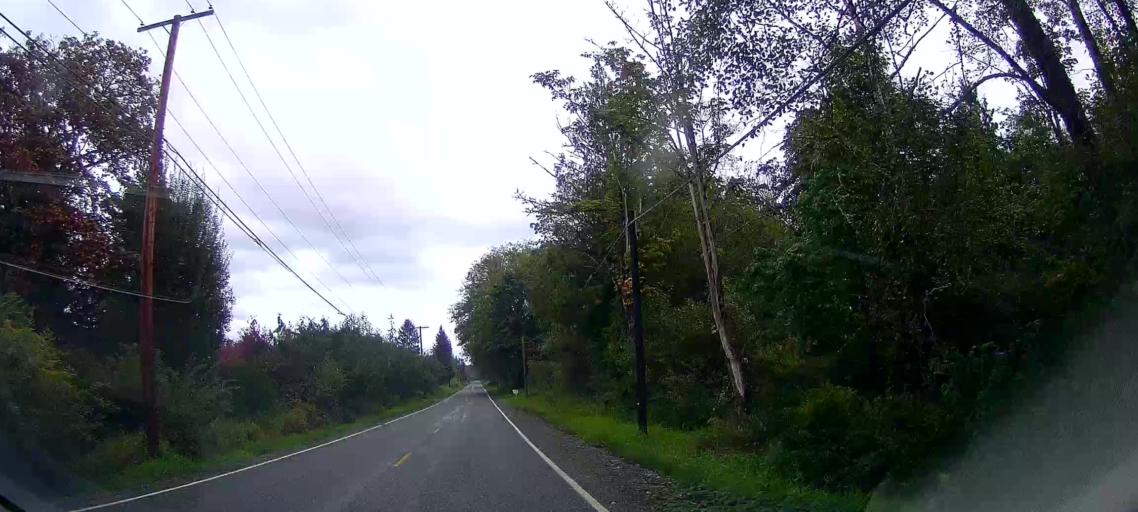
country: US
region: Washington
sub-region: Skagit County
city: Sedro-Woolley
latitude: 48.5274
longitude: -122.0473
